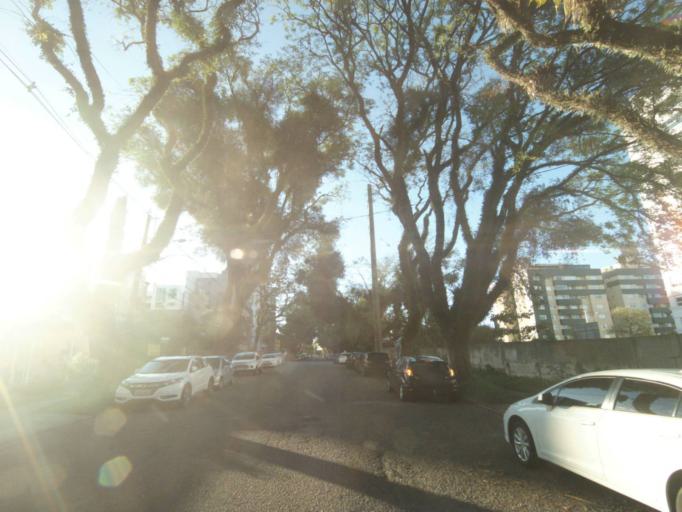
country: BR
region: Parana
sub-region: Curitiba
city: Curitiba
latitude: -25.3980
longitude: -49.2451
